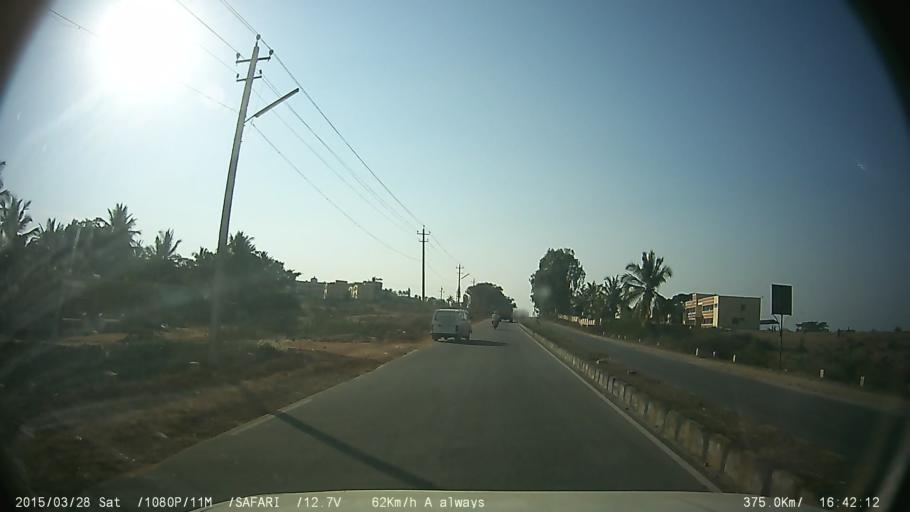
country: IN
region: Karnataka
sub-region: Mandya
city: Shrirangapattana
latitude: 12.4001
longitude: 76.5777
